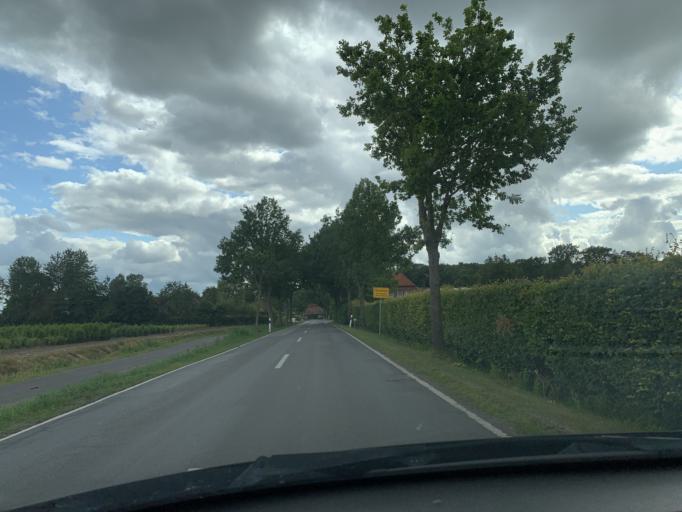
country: DE
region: Lower Saxony
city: Westerstede
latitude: 53.2160
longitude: 7.9366
